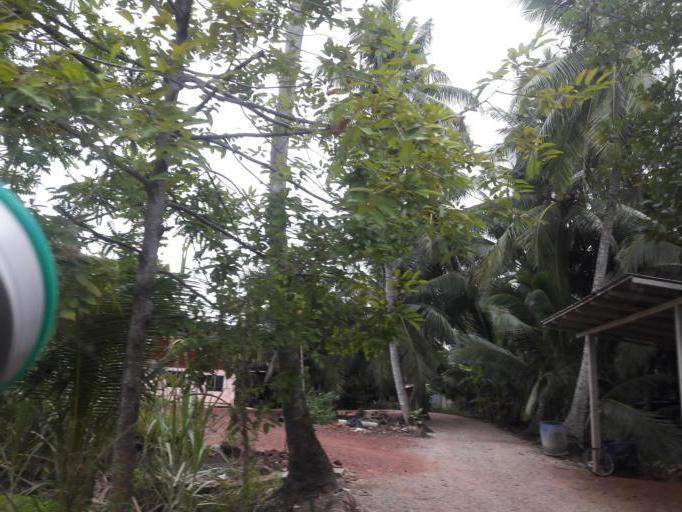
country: TH
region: Ratchaburi
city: Damnoen Saduak
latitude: 13.5071
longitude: 100.0219
